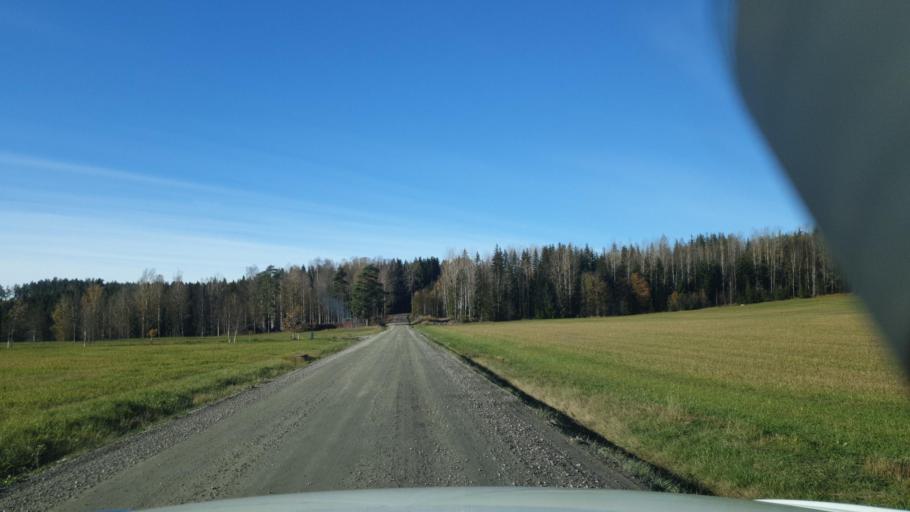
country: SE
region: Vaermland
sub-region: Karlstads Kommun
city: Edsvalla
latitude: 59.4867
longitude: 13.0435
